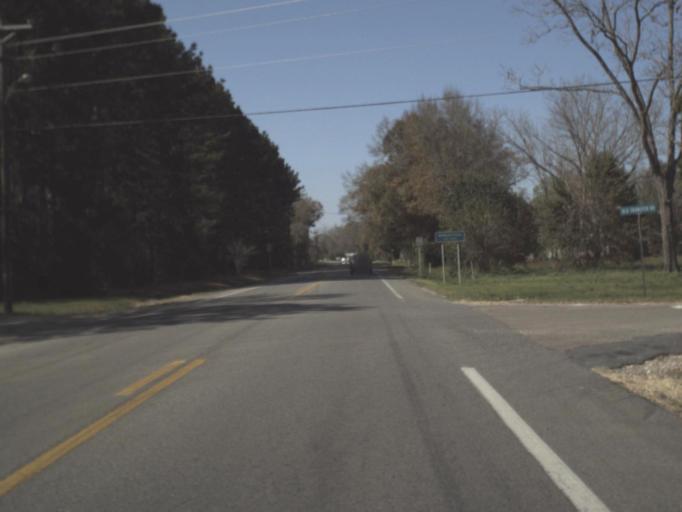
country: US
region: Florida
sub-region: Gulf County
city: Wewahitchka
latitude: 30.0914
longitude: -85.1956
